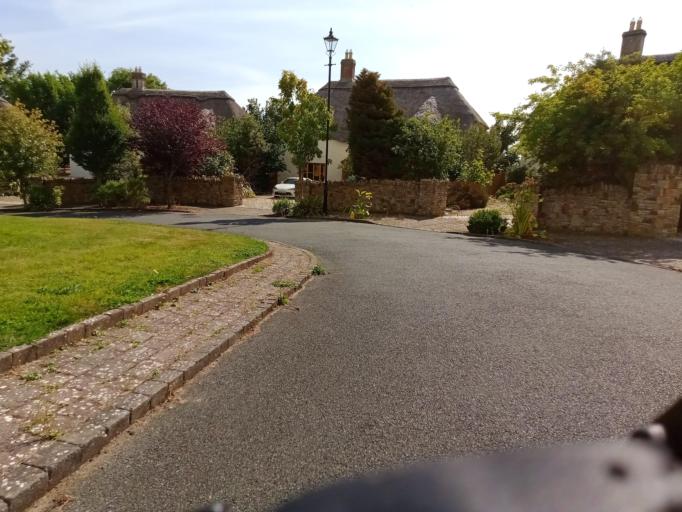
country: IE
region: Munster
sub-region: Waterford
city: Dungarvan
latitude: 52.1306
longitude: -7.4642
